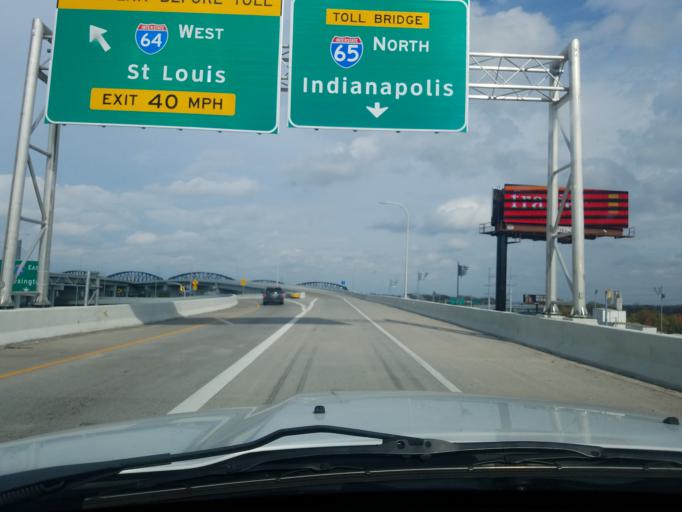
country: US
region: Kentucky
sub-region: Jefferson County
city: Louisville
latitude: 38.2565
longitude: -85.7411
